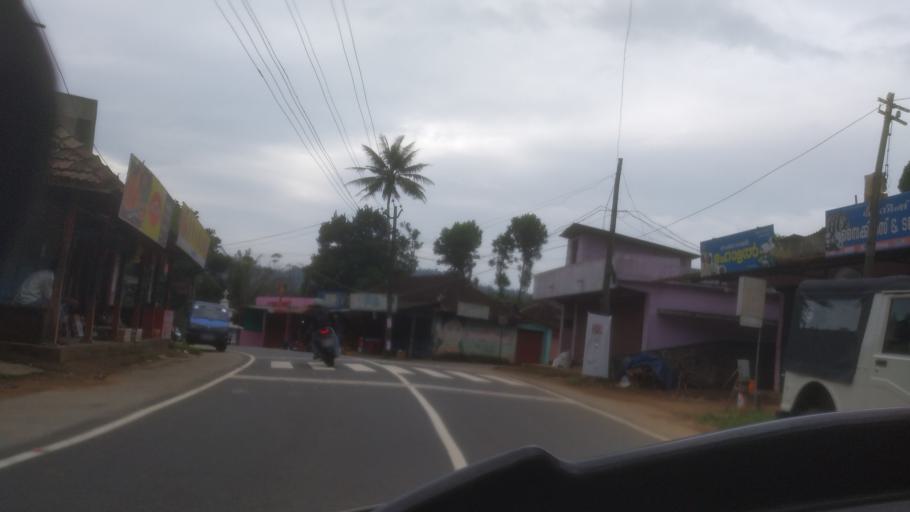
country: IN
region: Kerala
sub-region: Idukki
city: Idukki
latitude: 9.9532
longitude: 77.0118
